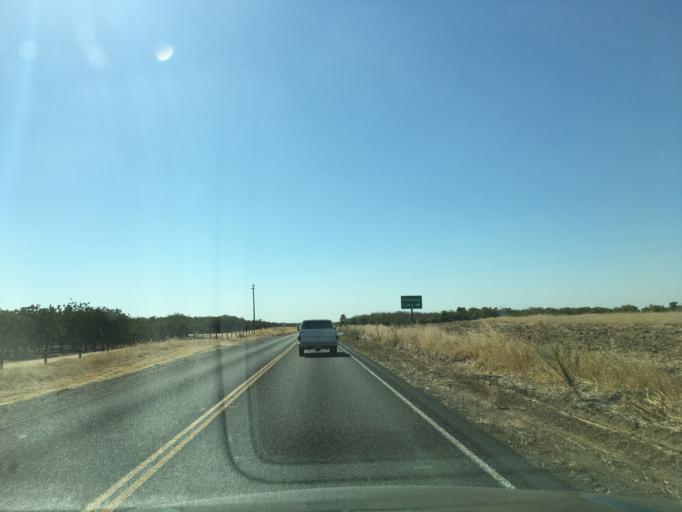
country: US
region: California
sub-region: Madera County
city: Bonadelle Ranchos-Madera Ranchos
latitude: 37.0095
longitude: -119.9453
